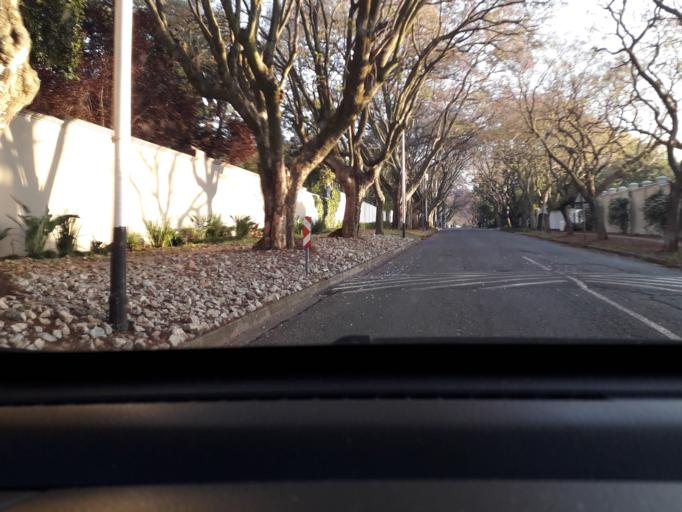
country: ZA
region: Gauteng
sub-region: City of Johannesburg Metropolitan Municipality
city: Johannesburg
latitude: -26.1421
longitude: 28.0510
